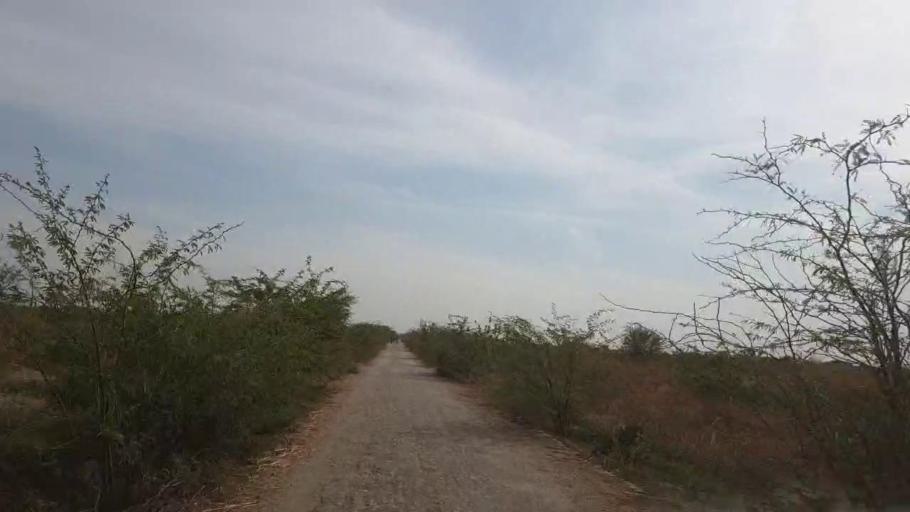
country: PK
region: Sindh
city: Nabisar
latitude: 25.0160
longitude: 69.5622
